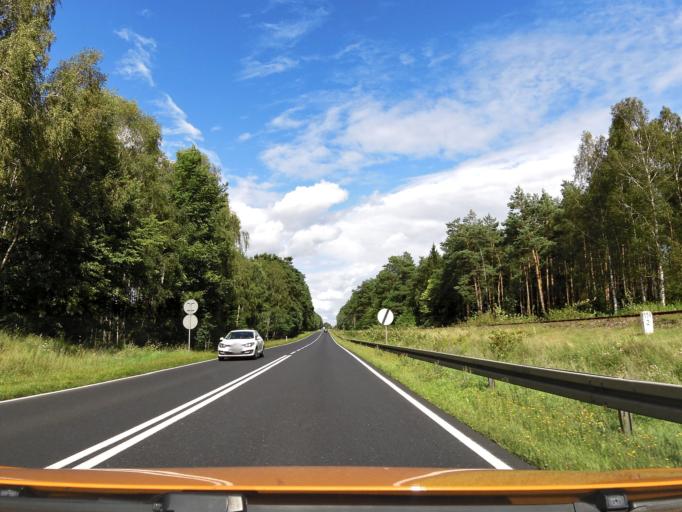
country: PL
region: West Pomeranian Voivodeship
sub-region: Powiat goleniowski
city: Nowogard
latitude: 53.6938
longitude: 15.1551
